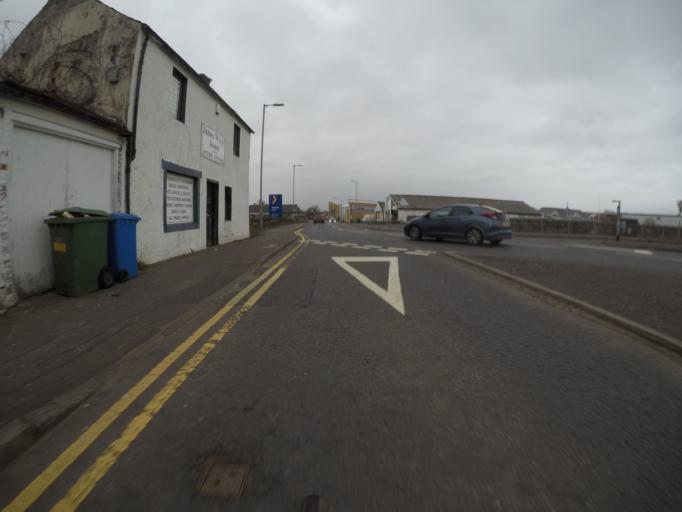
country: GB
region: Scotland
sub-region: North Ayrshire
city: Irvine
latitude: 55.6180
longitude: -4.6684
